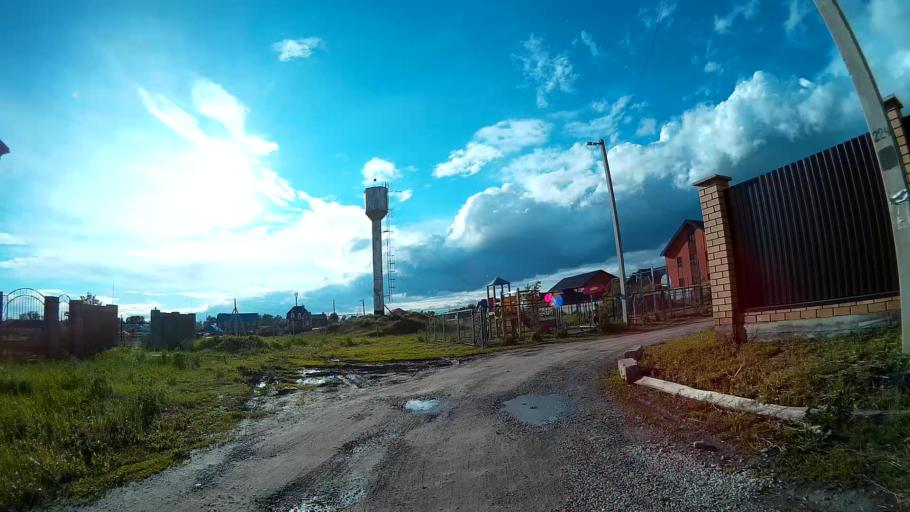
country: RU
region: Ulyanovsk
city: Novoul'yanovsk
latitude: 54.2032
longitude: 48.2739
